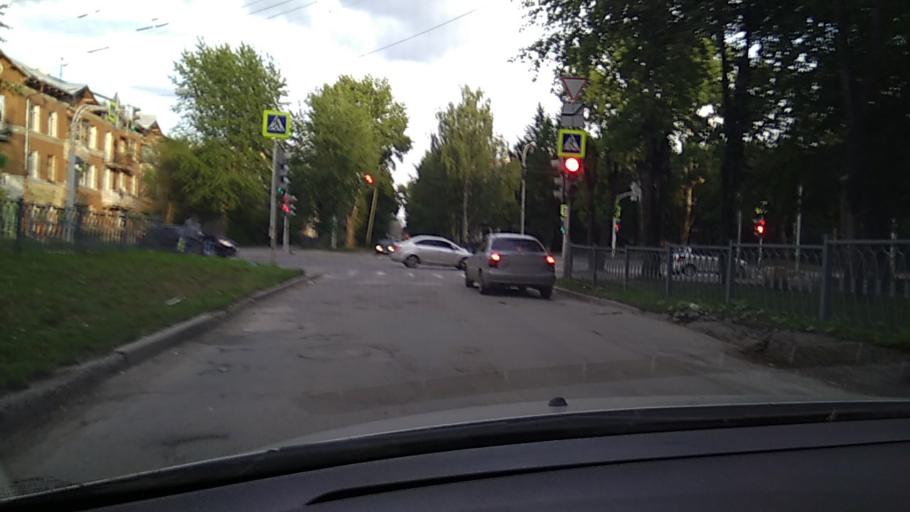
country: RU
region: Sverdlovsk
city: Yekaterinburg
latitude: 56.9001
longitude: 60.5880
